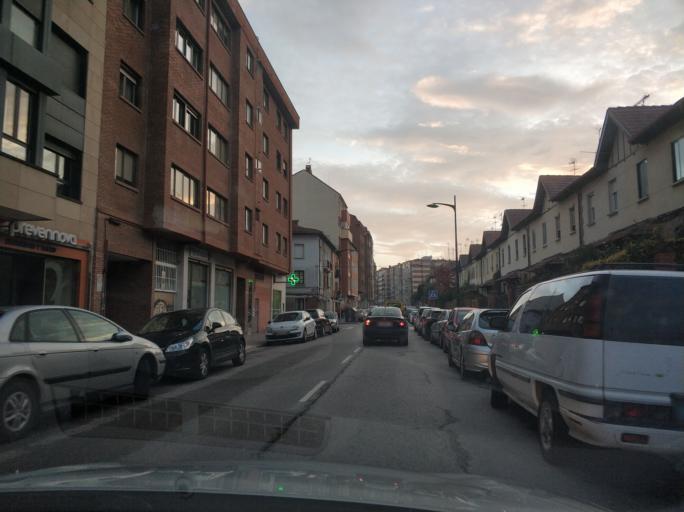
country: ES
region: Castille and Leon
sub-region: Provincia de Burgos
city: Burgos
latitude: 42.3486
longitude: -3.6995
